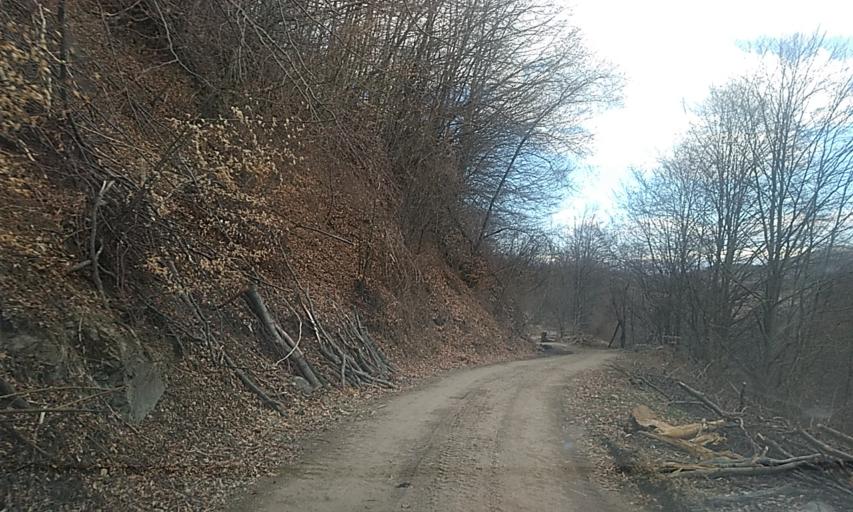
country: RS
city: Radovnica
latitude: 42.3491
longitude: 22.3395
